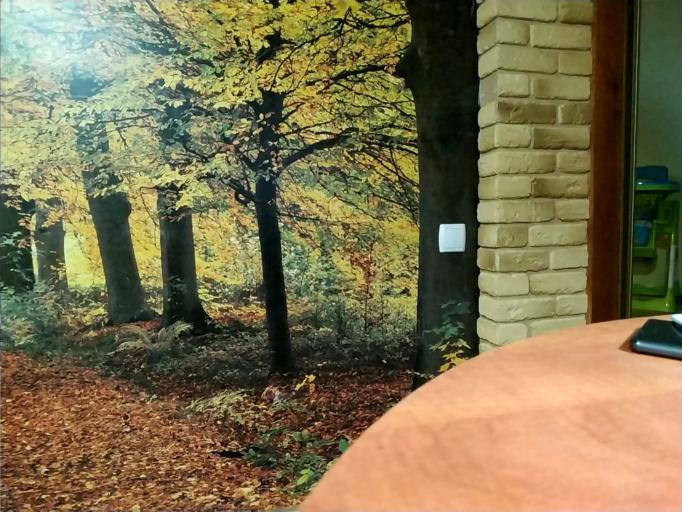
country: BY
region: Minsk
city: Plyeshchanitsy
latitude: 54.4287
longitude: 27.6417
